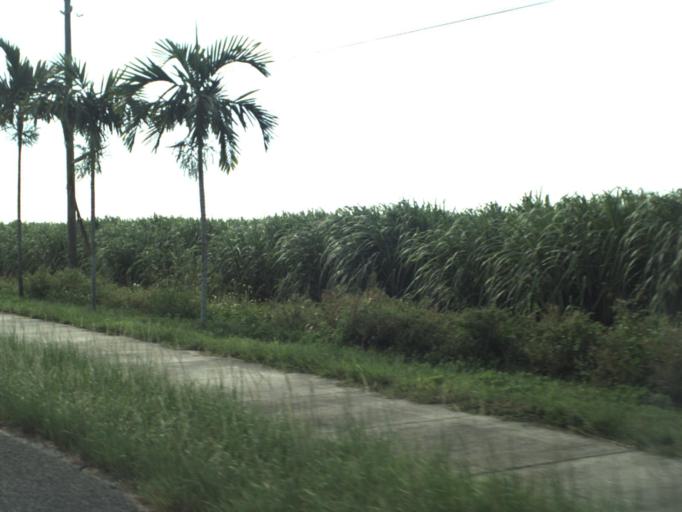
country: US
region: Florida
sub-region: Palm Beach County
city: South Bay
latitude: 26.6639
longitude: -80.7011
